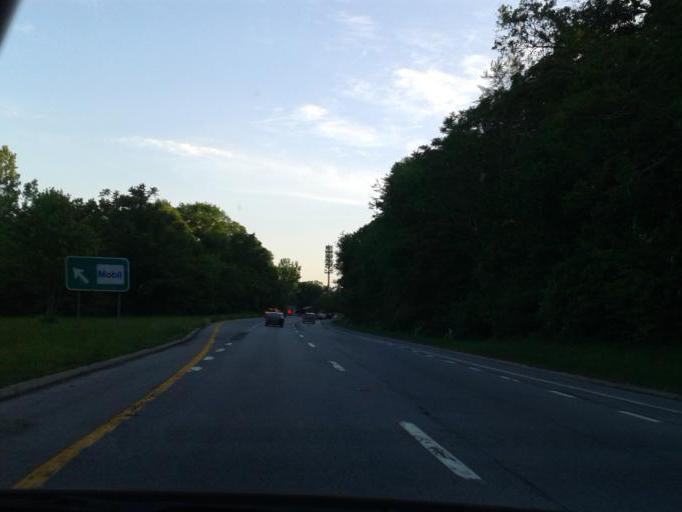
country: US
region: New York
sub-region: Westchester County
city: Harrison
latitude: 40.9963
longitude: -73.7295
